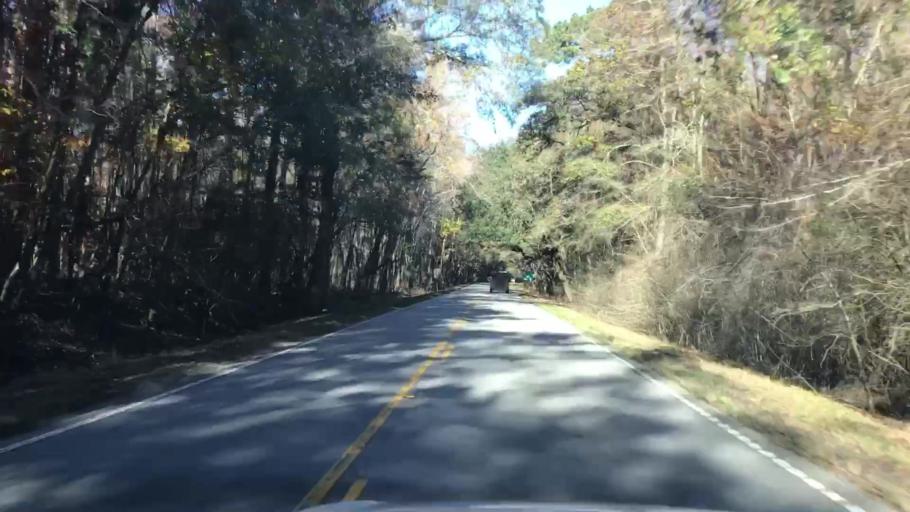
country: US
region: South Carolina
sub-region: Berkeley County
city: Ladson
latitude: 32.9106
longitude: -80.1502
